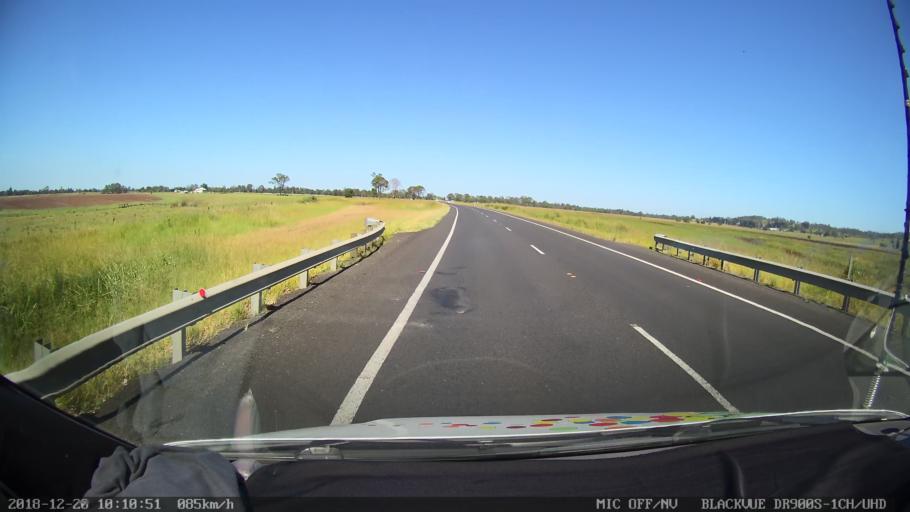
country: AU
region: New South Wales
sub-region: Richmond Valley
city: Casino
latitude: -28.8736
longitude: 153.1673
